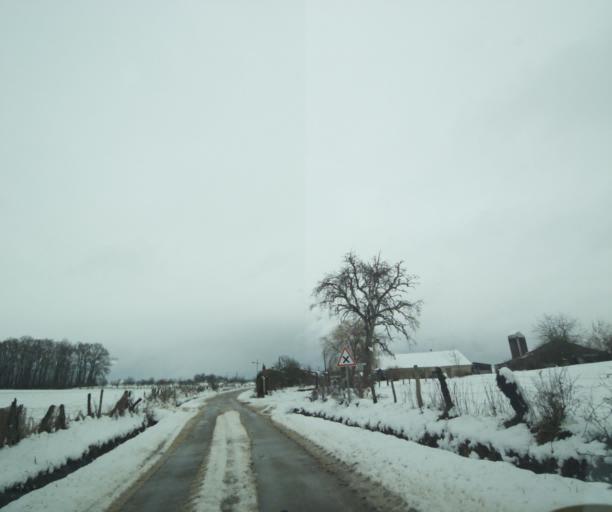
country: FR
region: Champagne-Ardenne
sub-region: Departement de la Haute-Marne
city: Montier-en-Der
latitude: 48.4219
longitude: 4.7858
